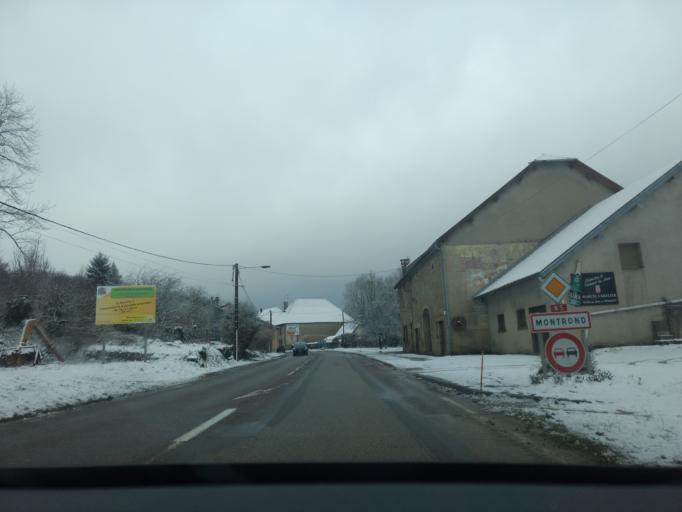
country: FR
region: Franche-Comte
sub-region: Departement du Jura
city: Champagnole
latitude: 46.8013
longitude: 5.8317
